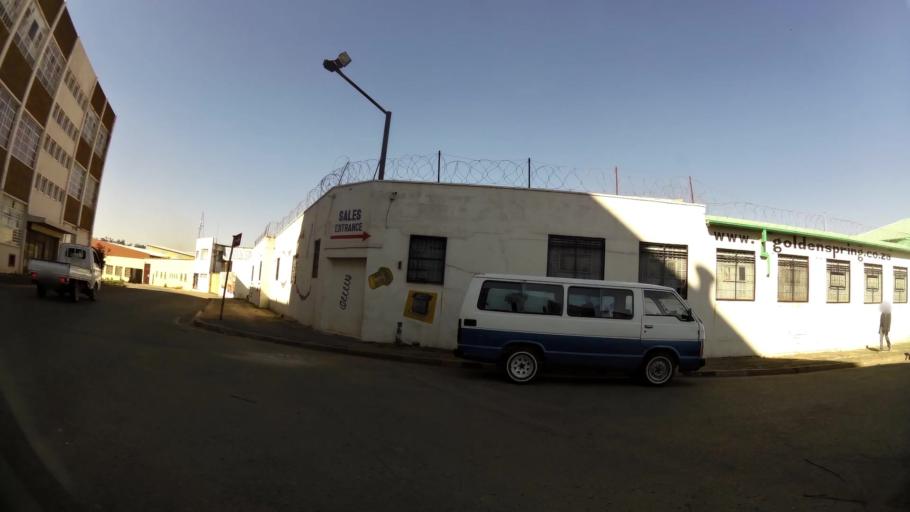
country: ZA
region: Gauteng
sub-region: City of Johannesburg Metropolitan Municipality
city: Johannesburg
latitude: -26.2140
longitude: 28.0475
